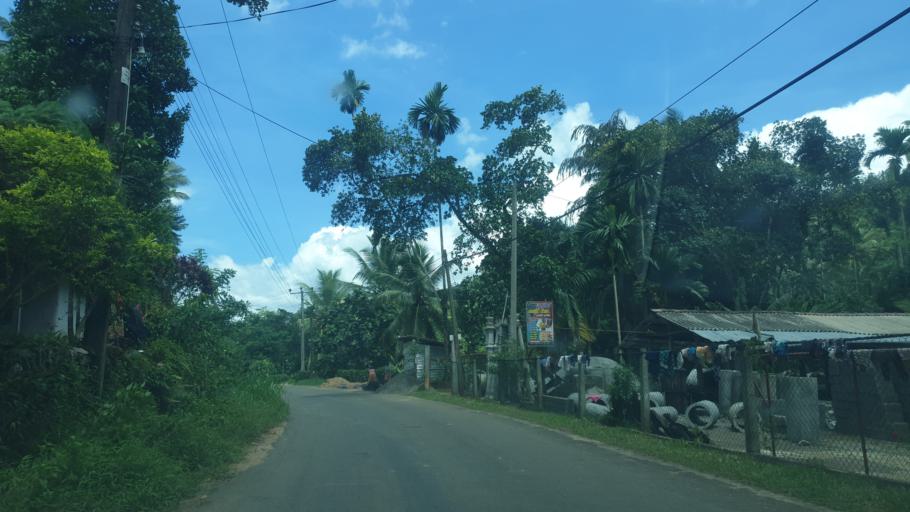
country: LK
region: Sabaragamuwa
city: Ratnapura
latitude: 6.4863
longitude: 80.4040
